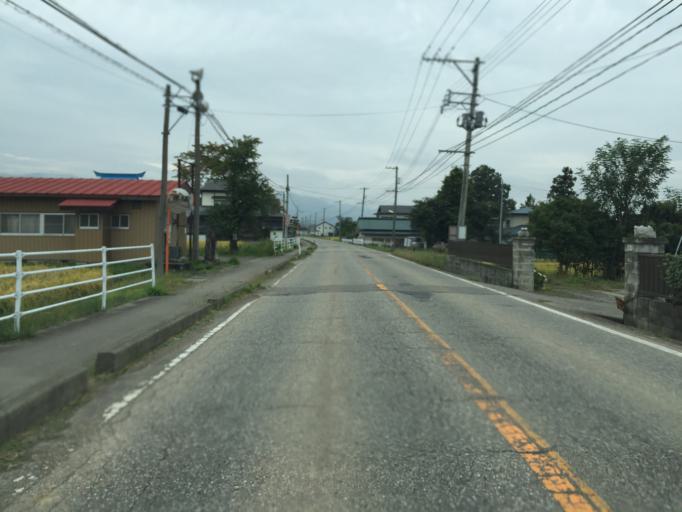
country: JP
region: Fukushima
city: Kitakata
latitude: 37.5383
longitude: 139.9296
